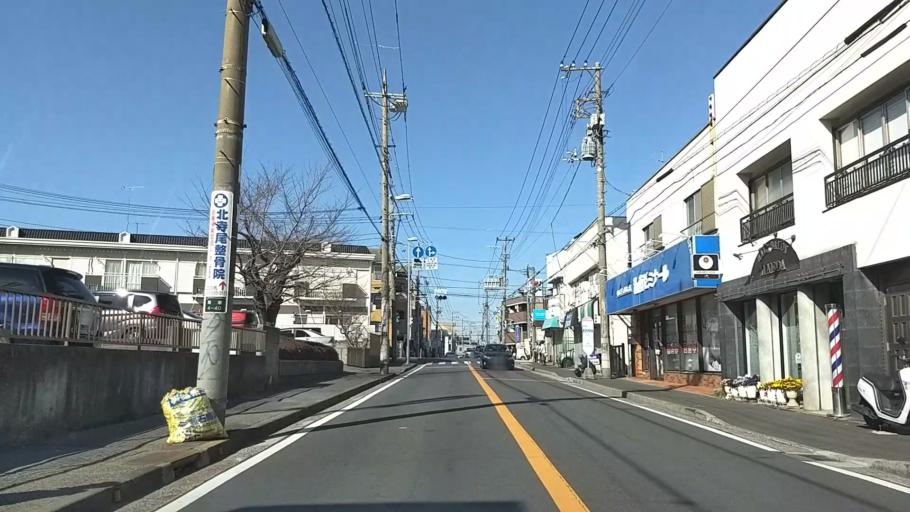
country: JP
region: Kanagawa
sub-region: Kawasaki-shi
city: Kawasaki
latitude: 35.5126
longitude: 139.6592
